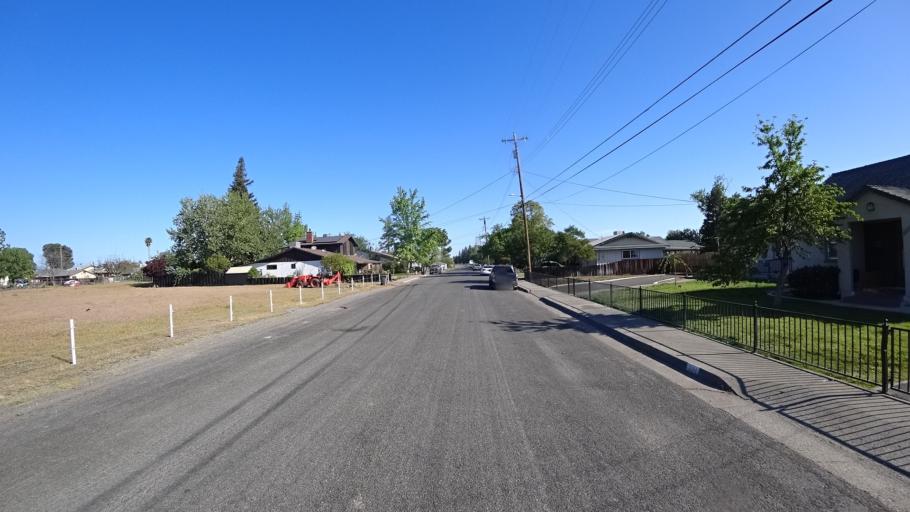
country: US
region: California
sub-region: Glenn County
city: Orland
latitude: 39.7517
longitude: -122.1850
